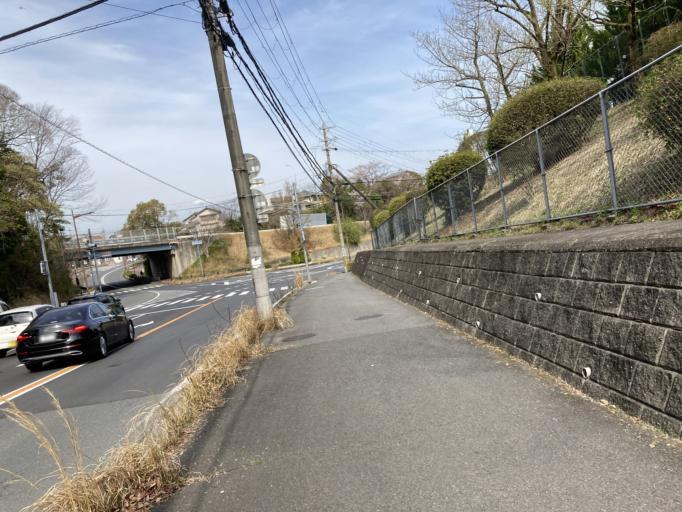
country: JP
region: Nara
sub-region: Ikoma-shi
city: Ikoma
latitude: 34.6879
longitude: 135.7227
